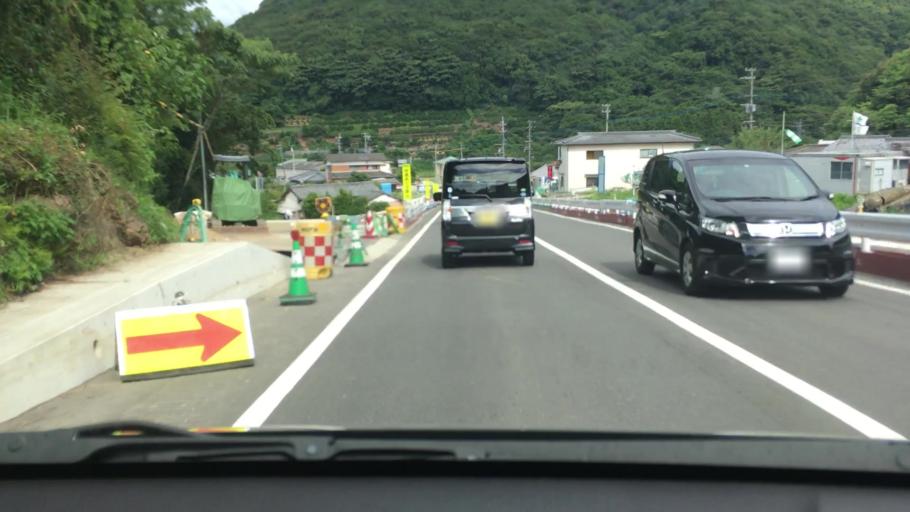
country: JP
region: Nagasaki
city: Togitsu
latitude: 32.8599
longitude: 129.8047
